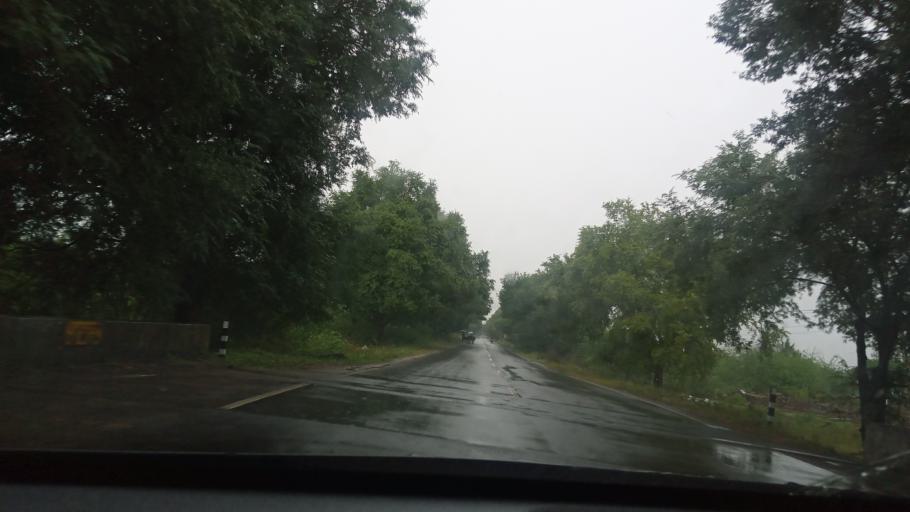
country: IN
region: Tamil Nadu
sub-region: Vellore
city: Kalavai
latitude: 12.8439
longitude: 79.3981
